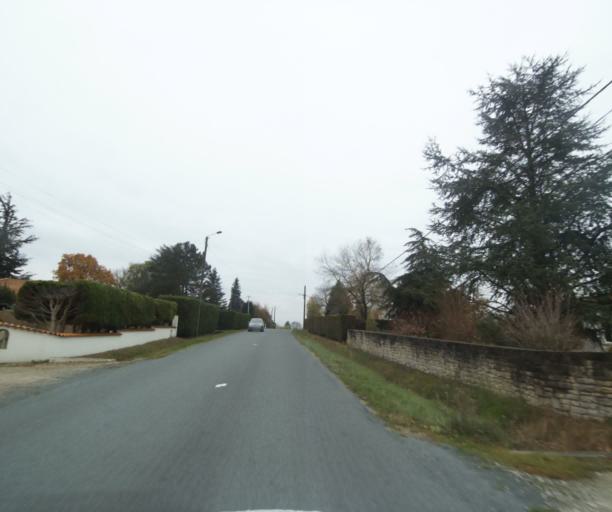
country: FR
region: Poitou-Charentes
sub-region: Departement de la Charente-Maritime
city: Saintes
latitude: 45.7271
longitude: -0.6670
